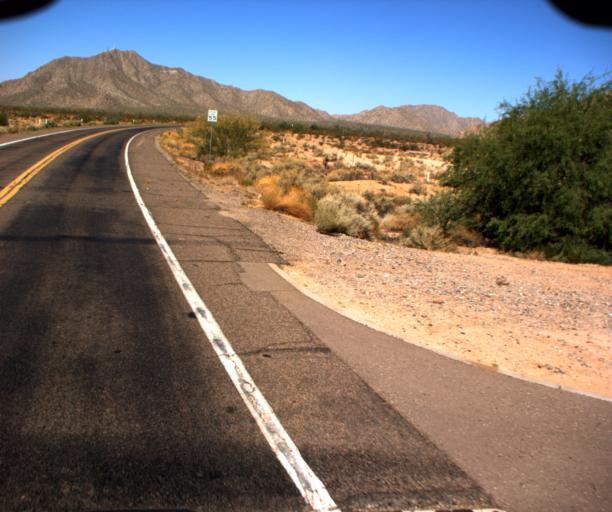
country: US
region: Arizona
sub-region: Pinal County
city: Blackwater
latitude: 33.0199
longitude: -111.6381
